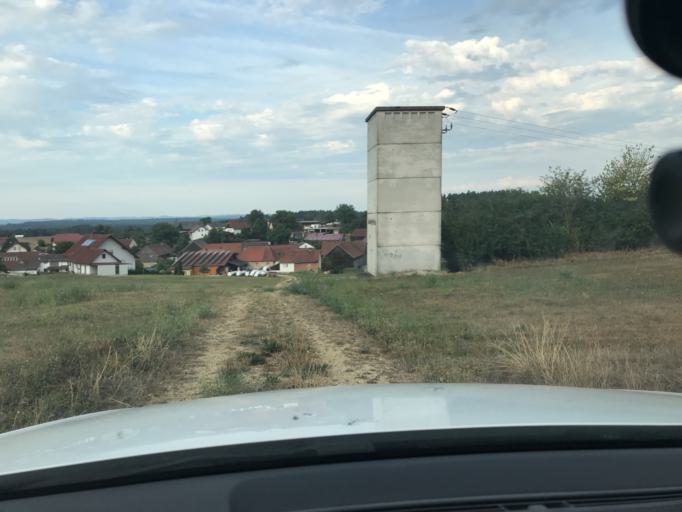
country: DE
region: Bavaria
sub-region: Upper Palatinate
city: Auerbach
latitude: 49.7230
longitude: 11.6204
